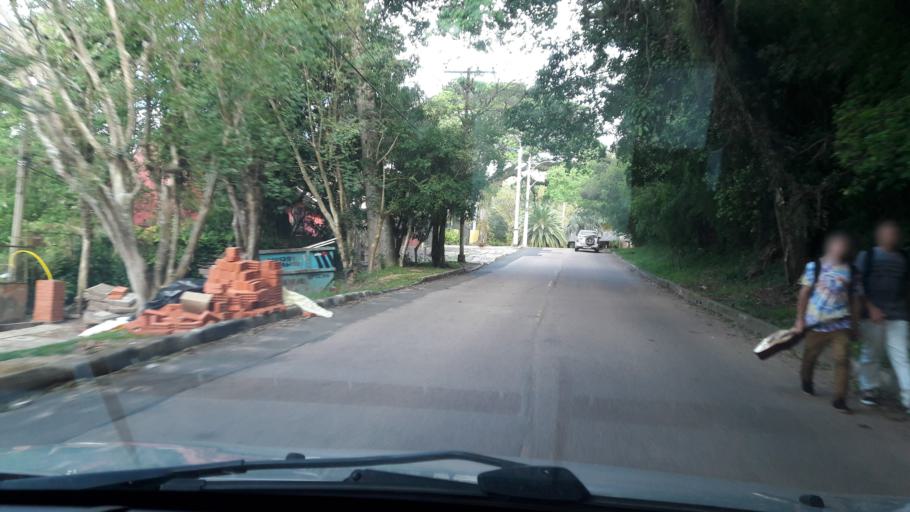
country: BR
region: Rio Grande do Sul
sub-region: Porto Alegre
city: Porto Alegre
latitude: -30.0850
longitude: -51.2024
